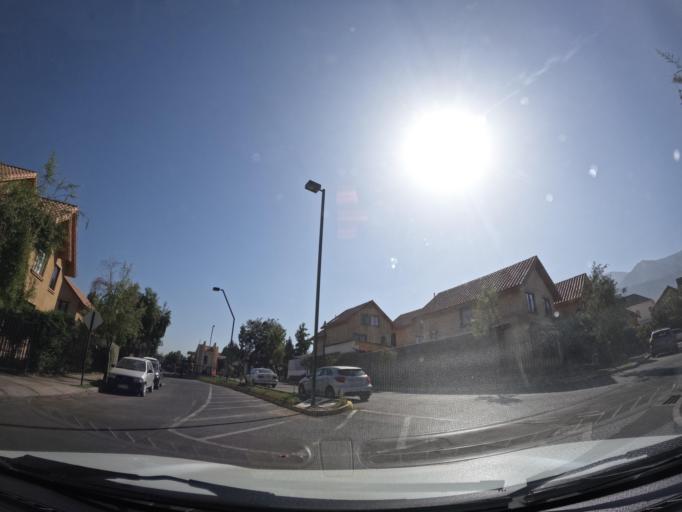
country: CL
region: Santiago Metropolitan
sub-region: Provincia de Santiago
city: Villa Presidente Frei, Nunoa, Santiago, Chile
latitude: -33.5088
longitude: -70.5480
